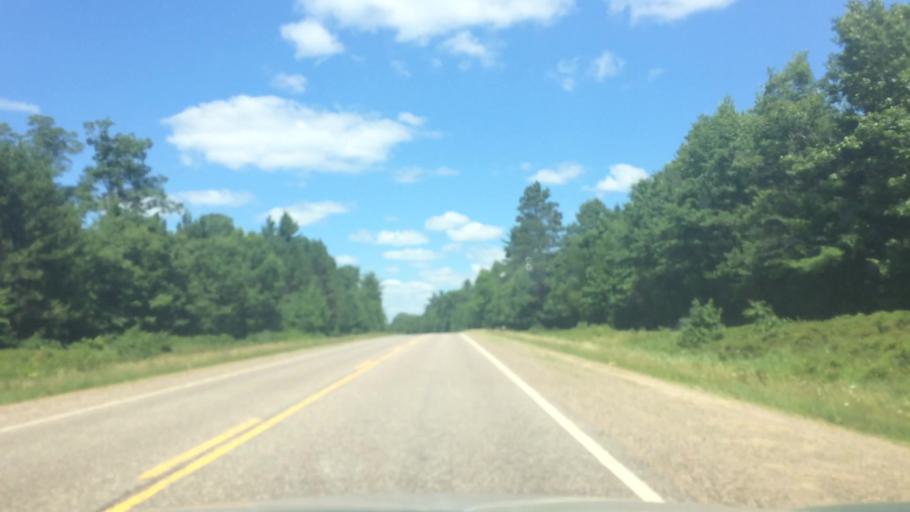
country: US
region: Wisconsin
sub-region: Vilas County
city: Lac du Flambeau
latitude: 46.0726
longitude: -89.6441
